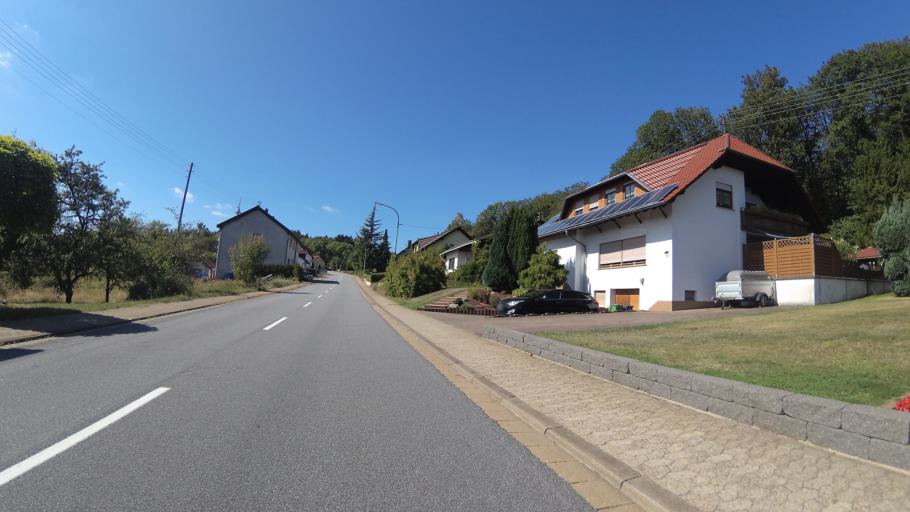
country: DE
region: Saarland
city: Lebach
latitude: 49.3908
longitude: 6.8904
